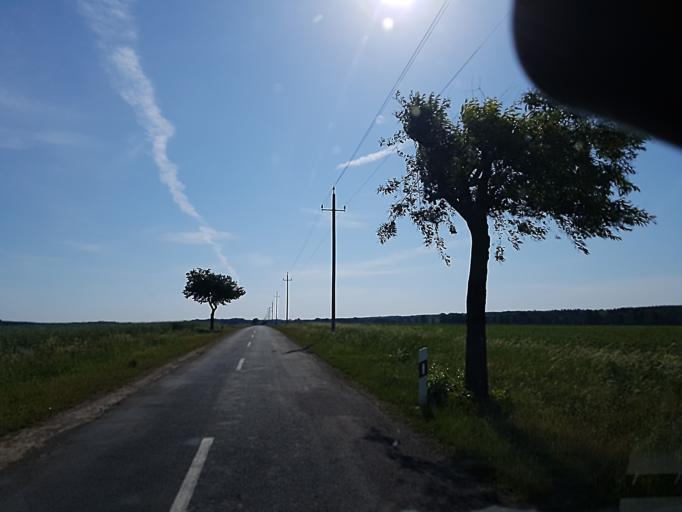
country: DE
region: Saxony-Anhalt
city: Rosslau
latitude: 52.0349
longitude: 12.2617
